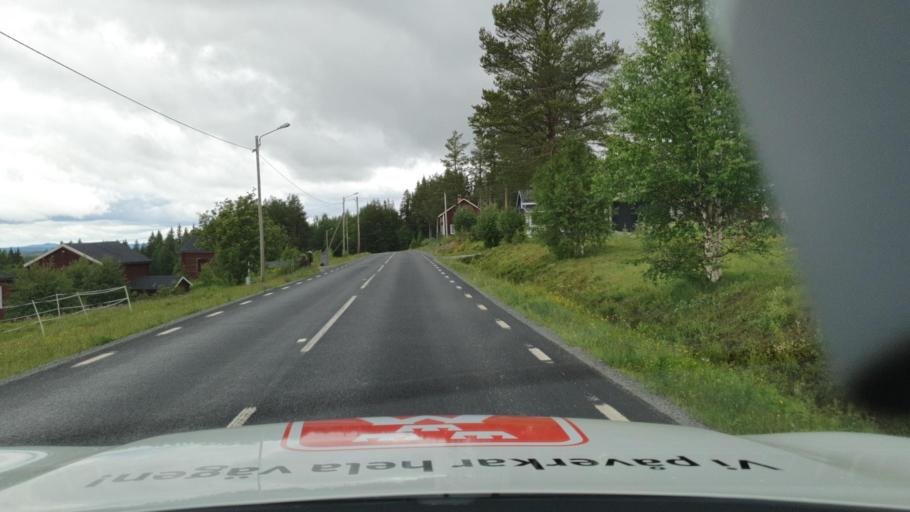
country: SE
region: Vaesterbotten
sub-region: Dorotea Kommun
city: Dorotea
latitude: 64.2365
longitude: 16.5414
